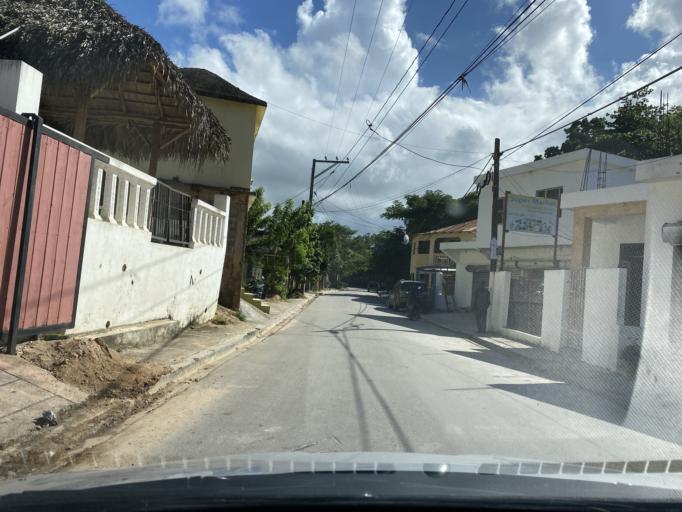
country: DO
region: Samana
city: Las Terrenas
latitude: 19.3163
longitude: -69.5300
